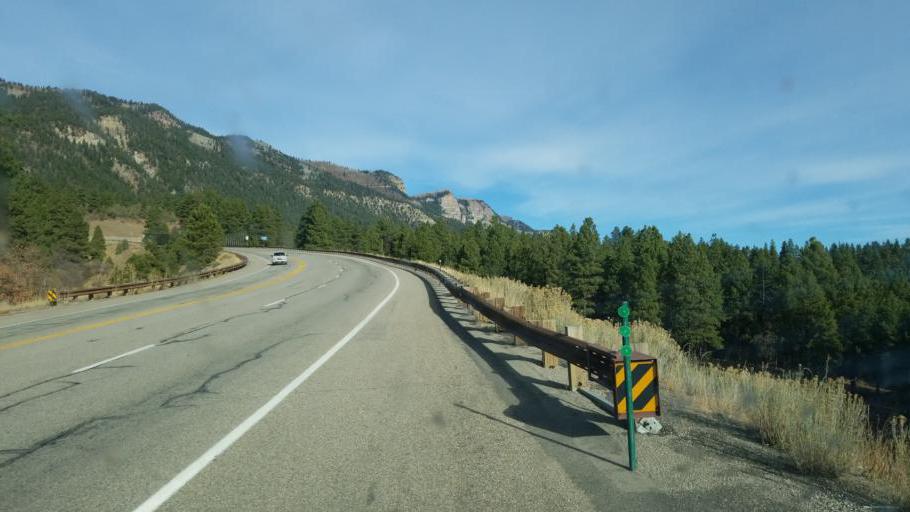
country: US
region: Colorado
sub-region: La Plata County
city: Durango
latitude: 37.4679
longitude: -107.8049
